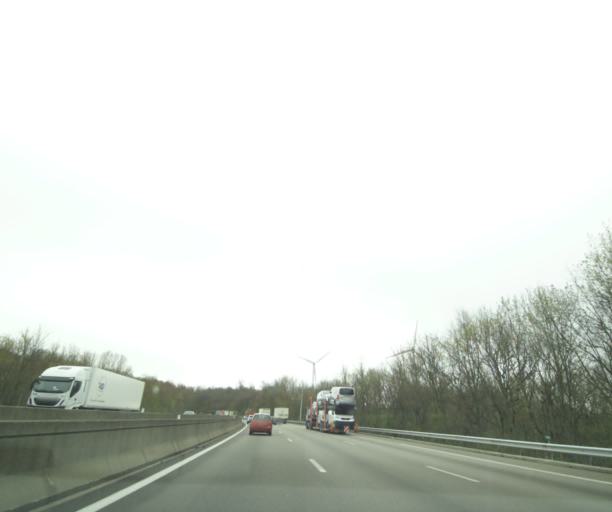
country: FR
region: Rhone-Alpes
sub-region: Departement de la Drome
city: Saint-Uze
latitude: 45.2133
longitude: 4.8622
